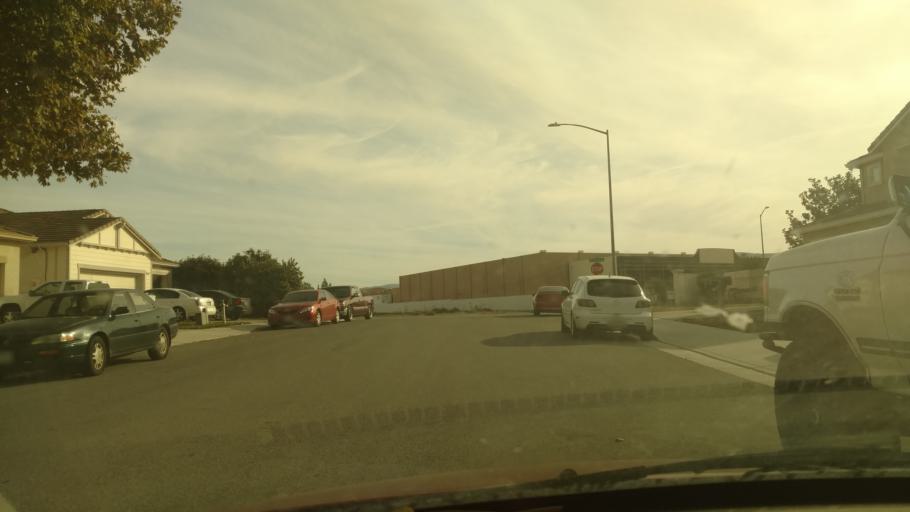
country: US
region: California
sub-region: San Benito County
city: Hollister
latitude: 36.8398
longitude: -121.3893
